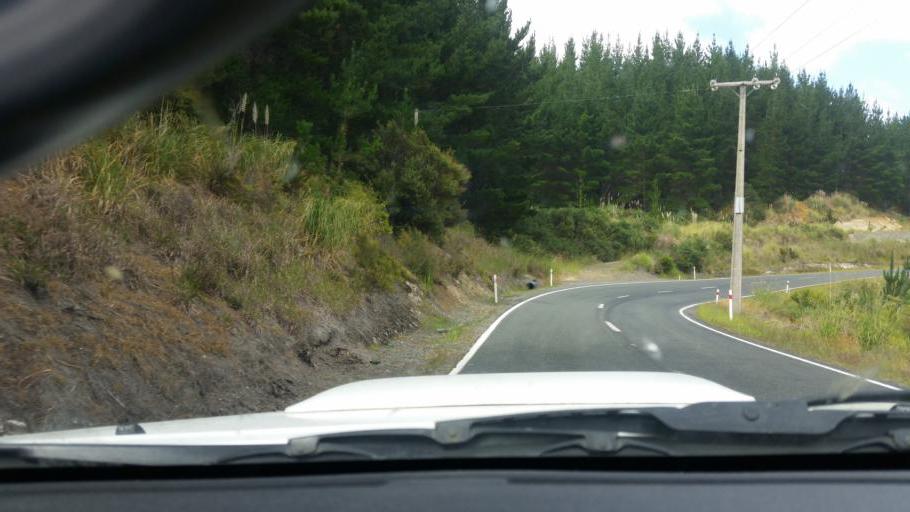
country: NZ
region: Northland
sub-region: Kaipara District
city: Dargaville
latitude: -35.8161
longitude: 173.7179
